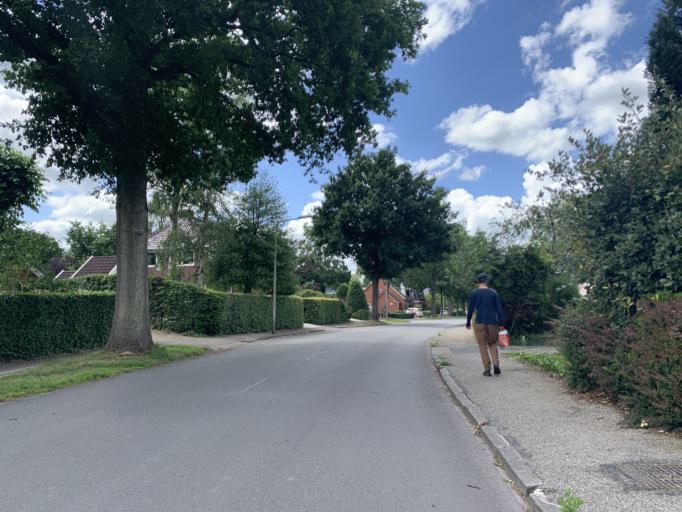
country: NL
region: Groningen
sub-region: Gemeente Haren
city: Haren
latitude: 53.1653
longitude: 6.6225
